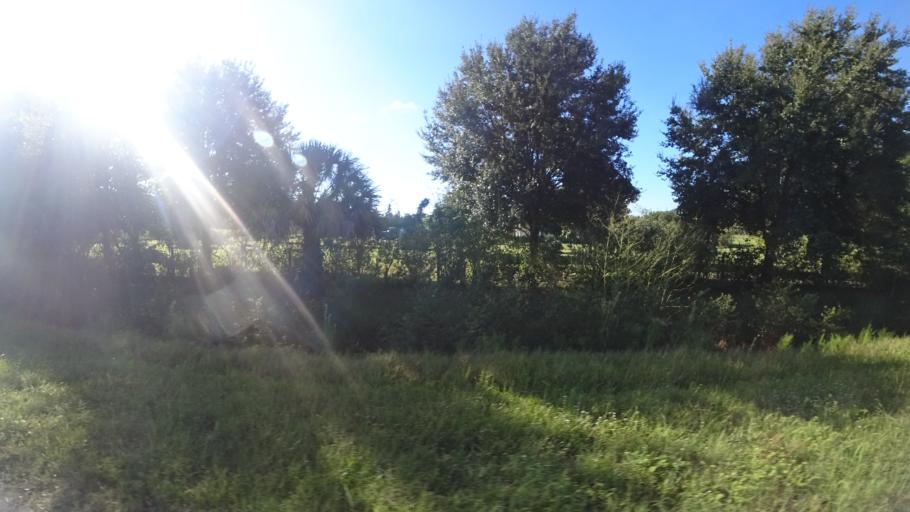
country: US
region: Florida
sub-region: Manatee County
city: Ellenton
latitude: 27.5831
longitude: -82.5206
